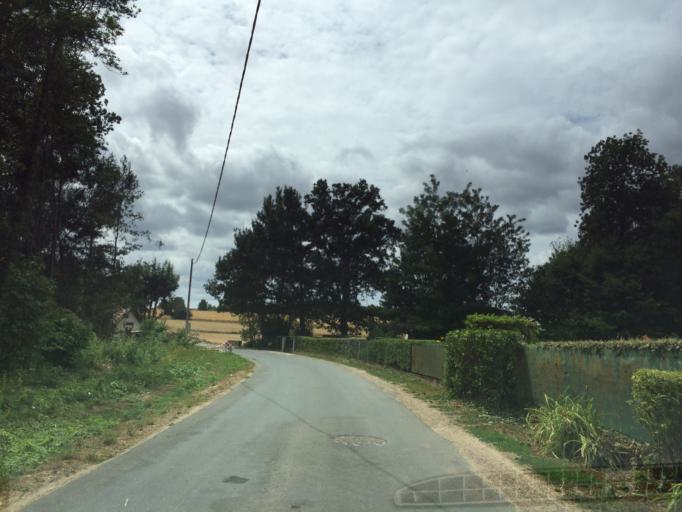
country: FR
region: Bourgogne
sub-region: Departement de l'Yonne
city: Fleury-la-Vallee
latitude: 47.8416
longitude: 3.4027
